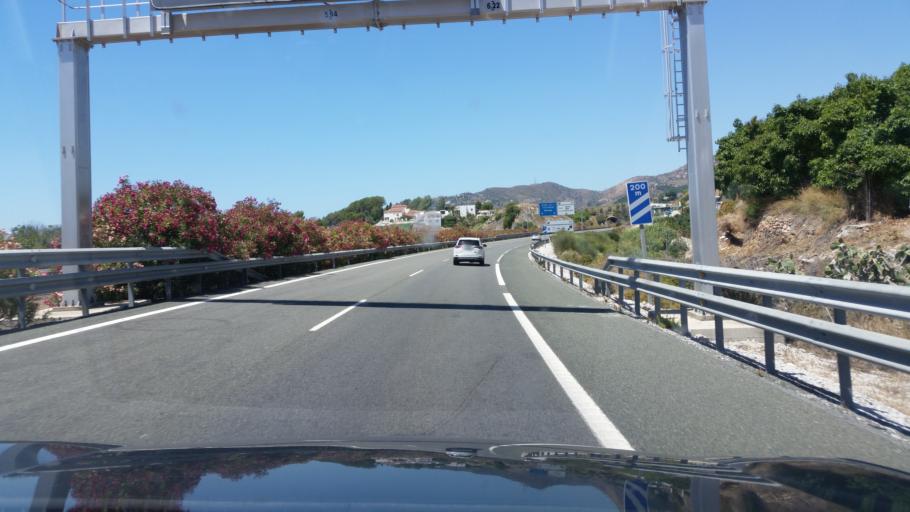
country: ES
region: Andalusia
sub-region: Provincia de Malaga
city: Nerja
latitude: 36.7646
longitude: -3.8795
